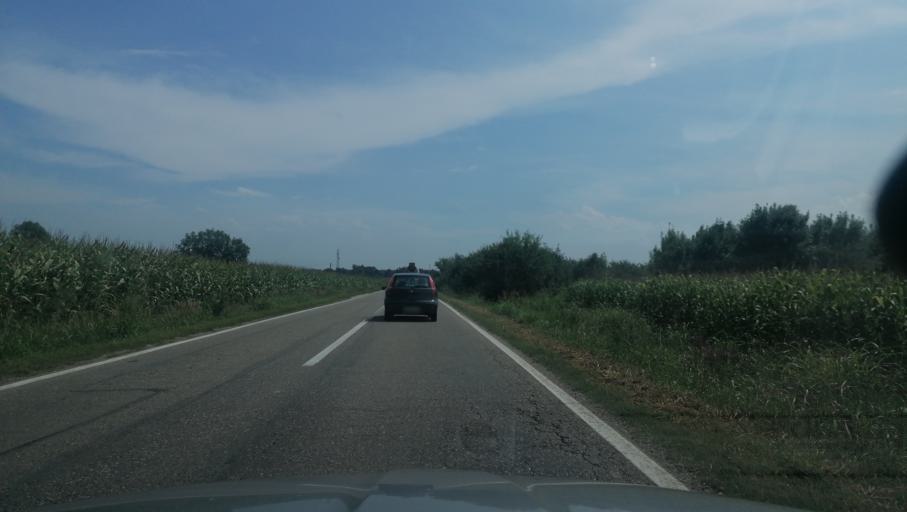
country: BA
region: Republika Srpska
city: Velika Obarska
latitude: 44.8191
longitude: 19.0520
